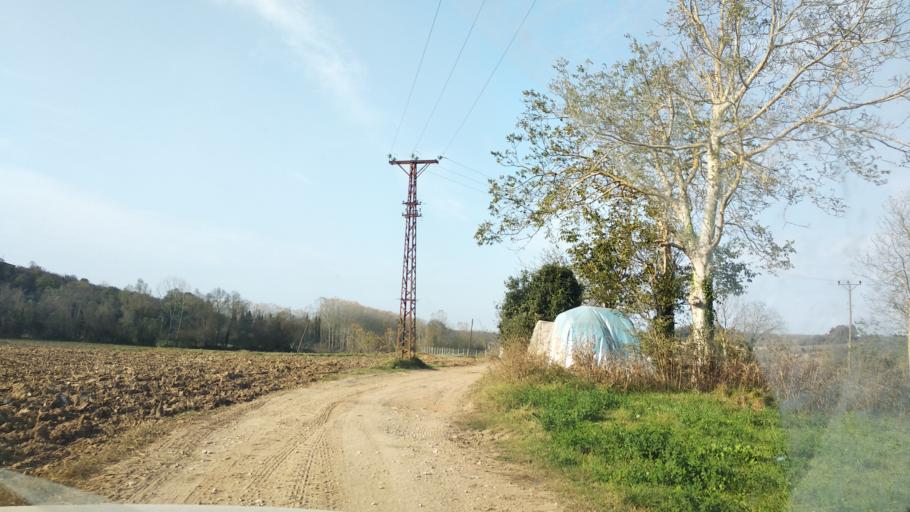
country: TR
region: Sakarya
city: Karasu
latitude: 41.0904
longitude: 30.5952
